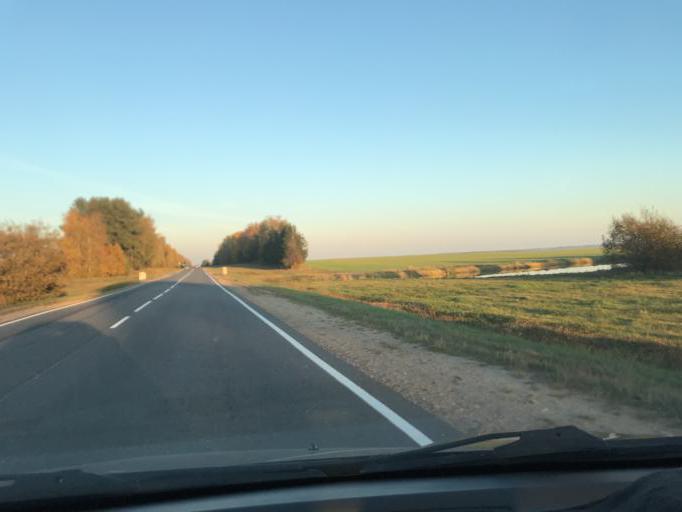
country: BY
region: Minsk
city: Staryya Darohi
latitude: 53.0604
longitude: 28.4831
